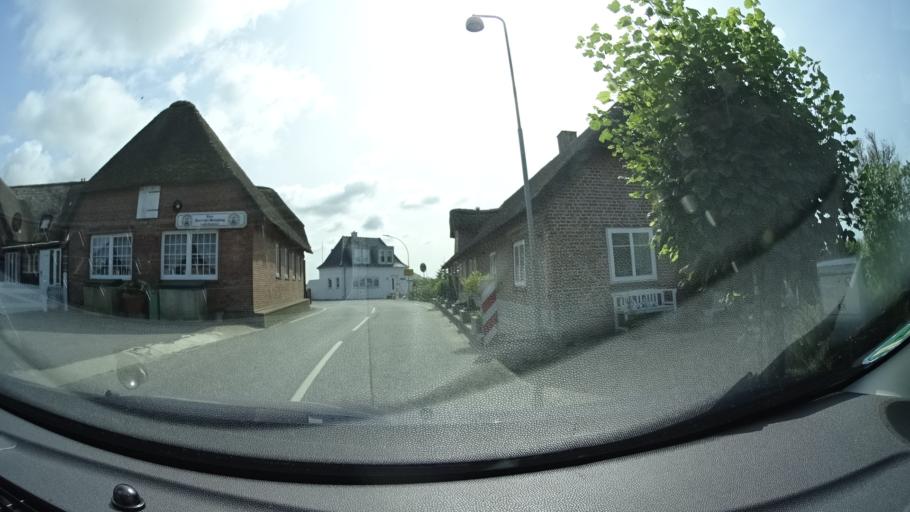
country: DE
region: Schleswig-Holstein
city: Neukirchen
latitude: 54.8957
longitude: 8.7499
